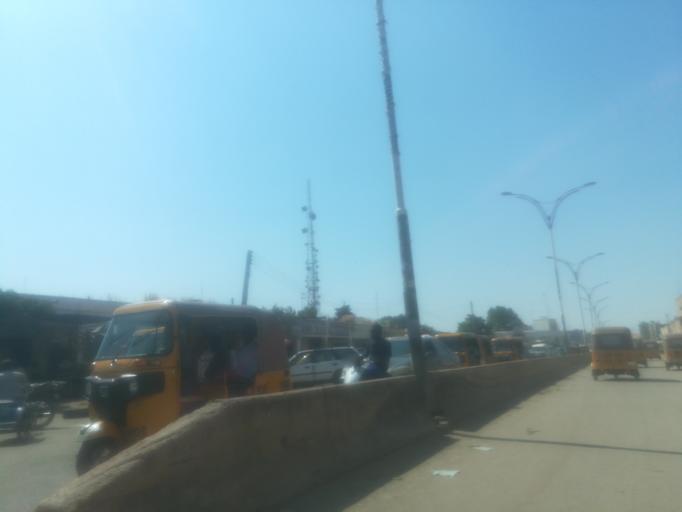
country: NG
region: Kano
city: Kano
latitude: 12.0080
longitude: 8.5401
